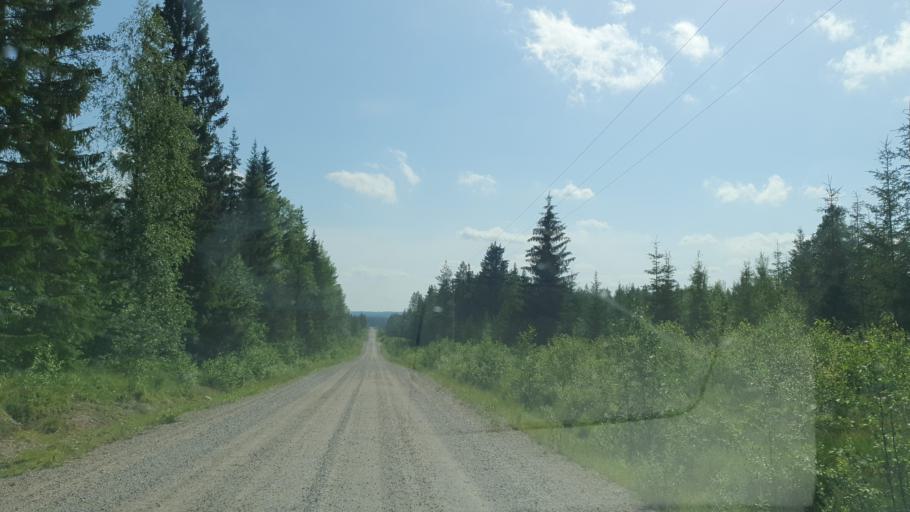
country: FI
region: Kainuu
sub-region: Kehys-Kainuu
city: Kuhmo
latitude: 64.0310
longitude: 29.9280
